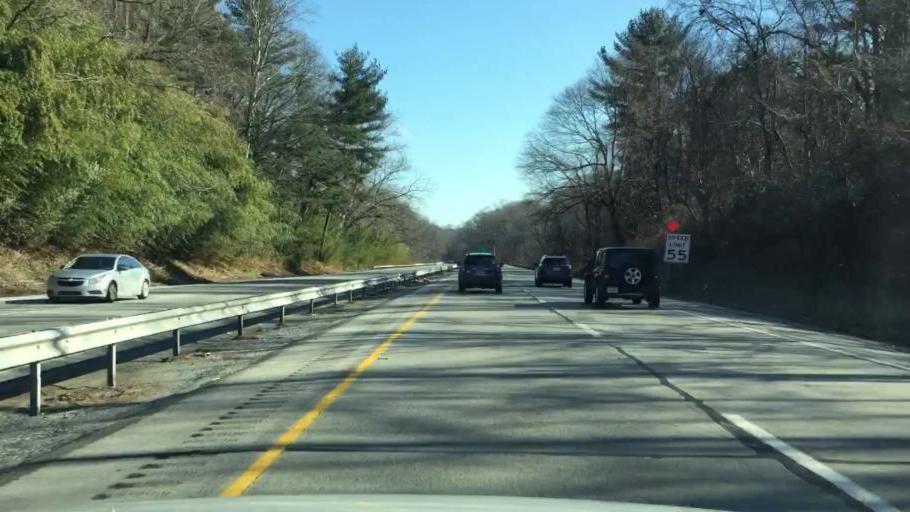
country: US
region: Pennsylvania
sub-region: Delaware County
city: Media
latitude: 39.9366
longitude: -75.3838
